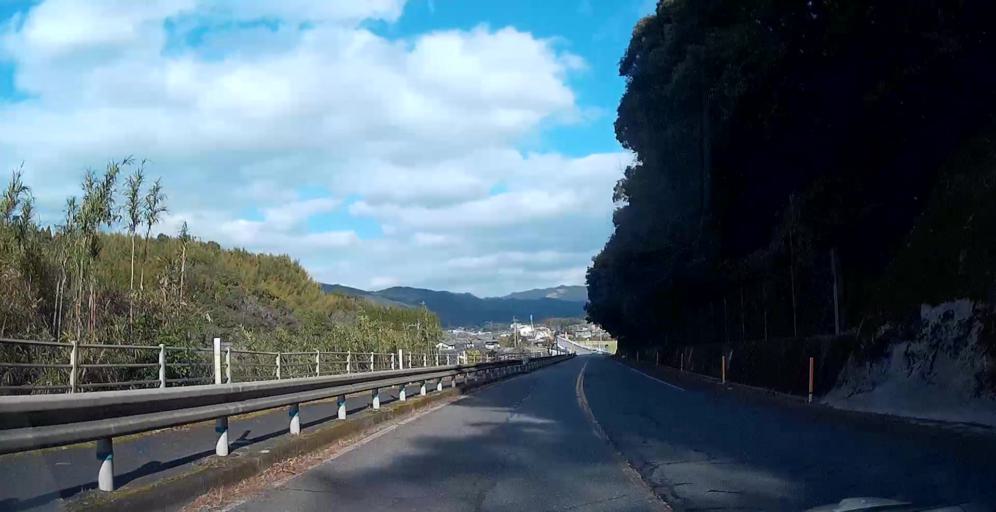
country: JP
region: Kumamoto
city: Yatsushiro
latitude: 32.3948
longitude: 130.5464
